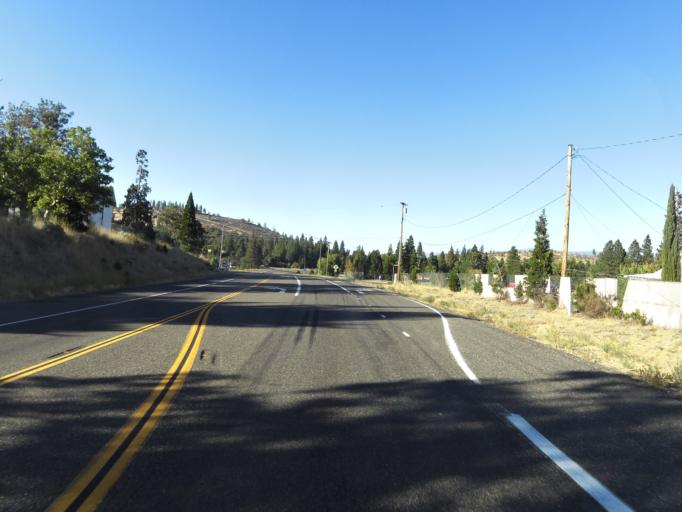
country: US
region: California
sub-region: Siskiyou County
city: Weed
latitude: 41.4356
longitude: -122.3870
